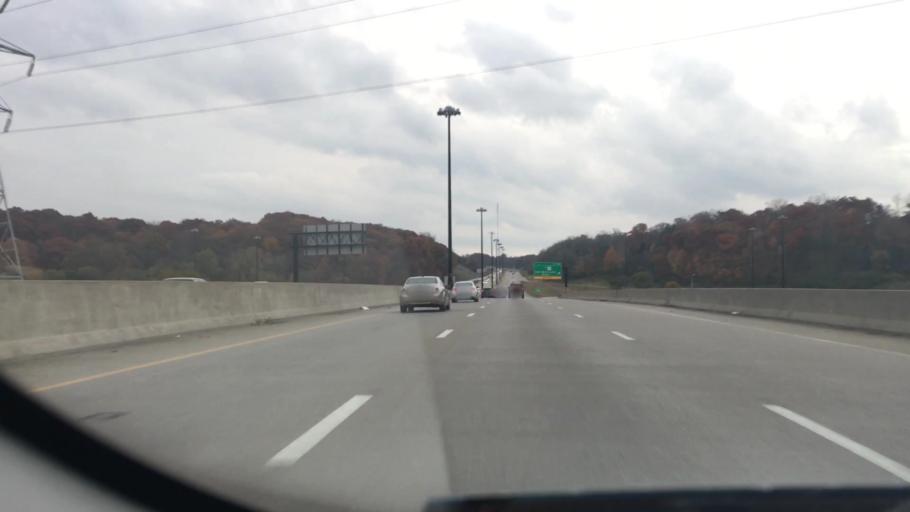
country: US
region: Illinois
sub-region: Tazewell County
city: East Peoria
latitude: 40.6654
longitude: -89.5702
